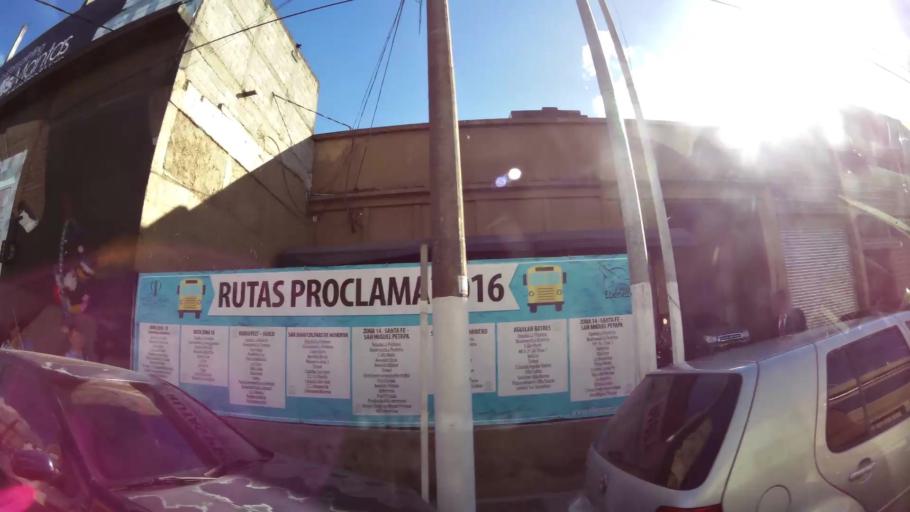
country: GT
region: Guatemala
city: Guatemala City
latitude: 14.6208
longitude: -90.5087
